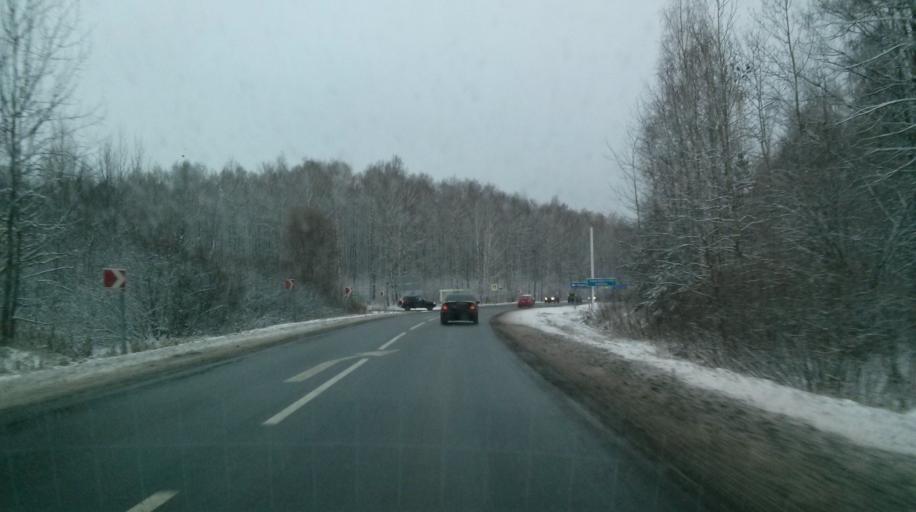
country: RU
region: Nizjnij Novgorod
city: Vorsma
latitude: 56.0138
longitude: 43.3440
